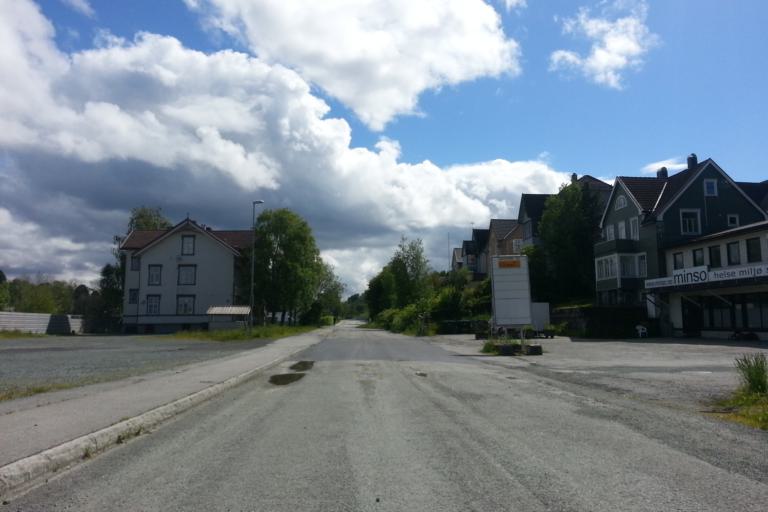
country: NO
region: Sor-Trondelag
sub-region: Trondheim
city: Trondheim
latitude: 63.4150
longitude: 10.3814
